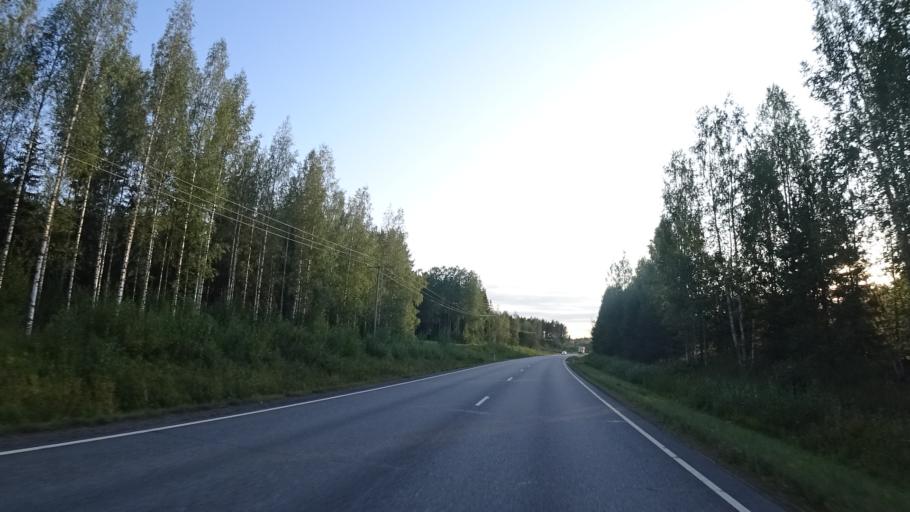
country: FI
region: South Karelia
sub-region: Lappeenranta
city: Ylaemaa
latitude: 60.7905
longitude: 28.0181
